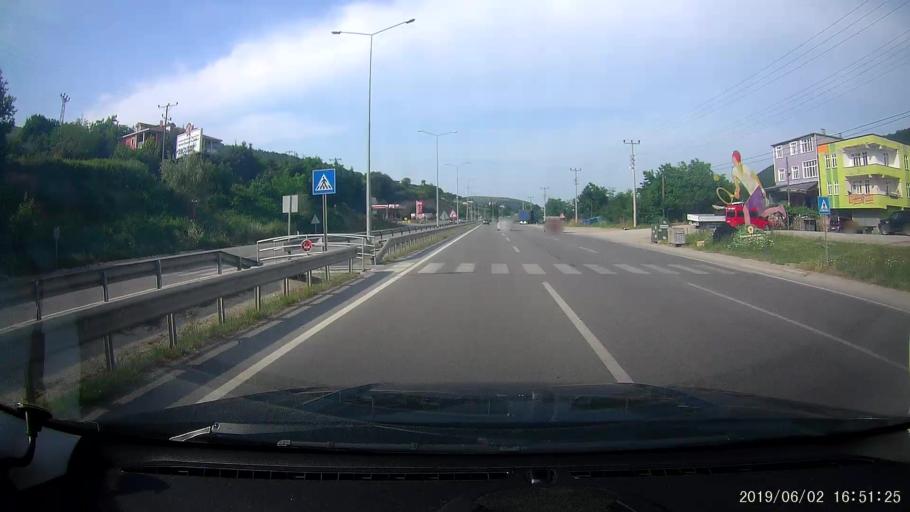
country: TR
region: Samsun
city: Taflan
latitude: 41.2735
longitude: 36.1821
